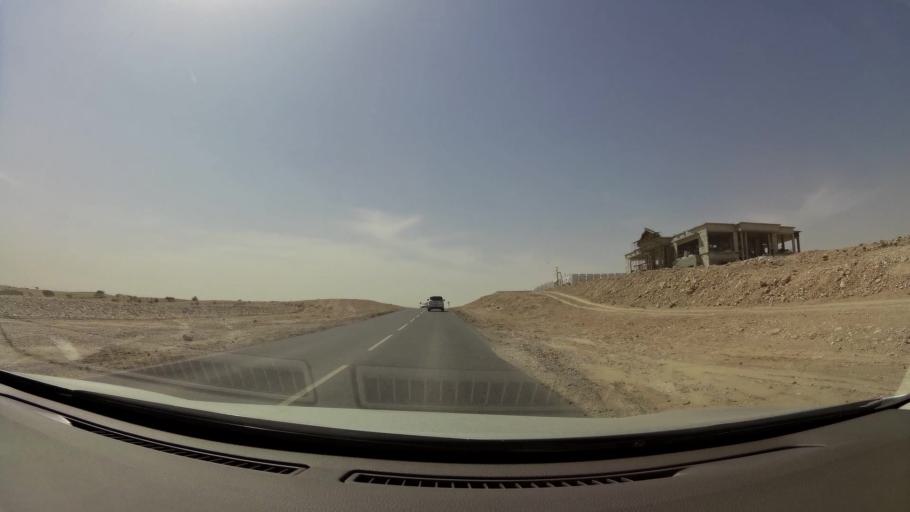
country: QA
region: Baladiyat ar Rayyan
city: Ar Rayyan
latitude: 25.2645
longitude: 51.3946
